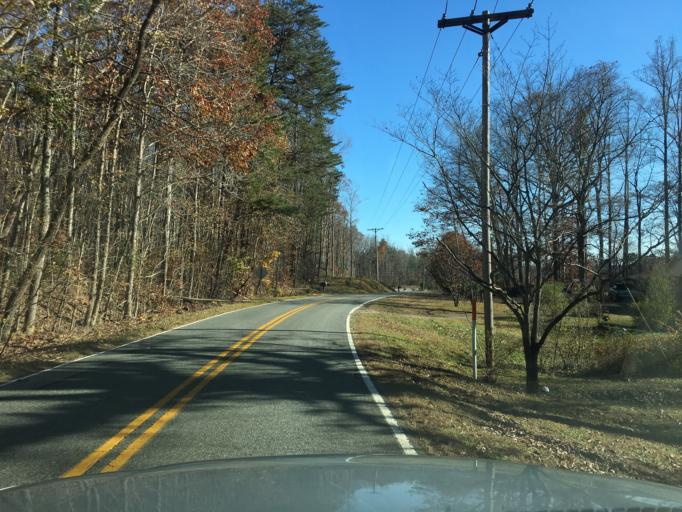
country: US
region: North Carolina
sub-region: Rutherford County
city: Rutherfordton
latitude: 35.2748
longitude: -82.0340
